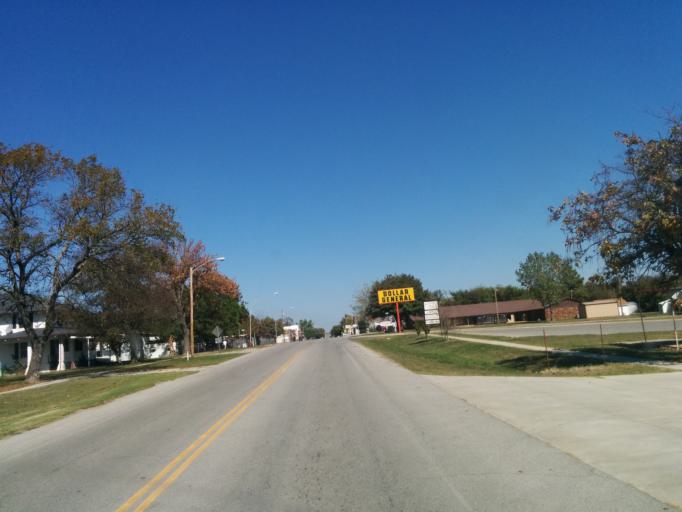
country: US
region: Oklahoma
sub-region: Creek County
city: Mounds
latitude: 35.8734
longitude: -96.0607
